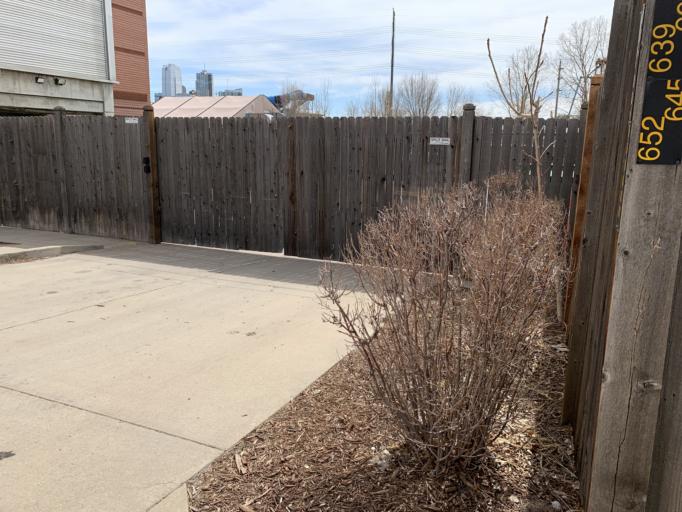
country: US
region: Colorado
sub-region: Denver County
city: Denver
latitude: 39.7516
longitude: -105.0146
